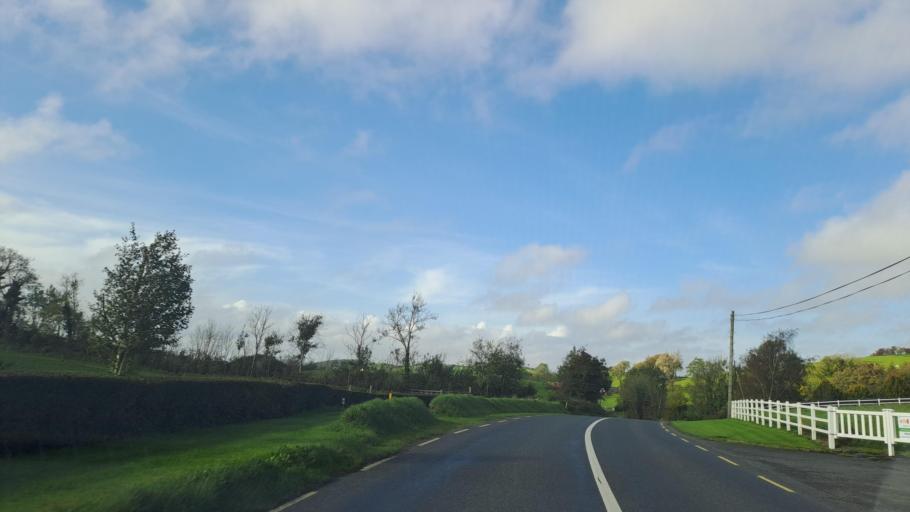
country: IE
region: Ulster
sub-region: An Cabhan
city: Cootehill
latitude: 54.0610
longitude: -7.0343
